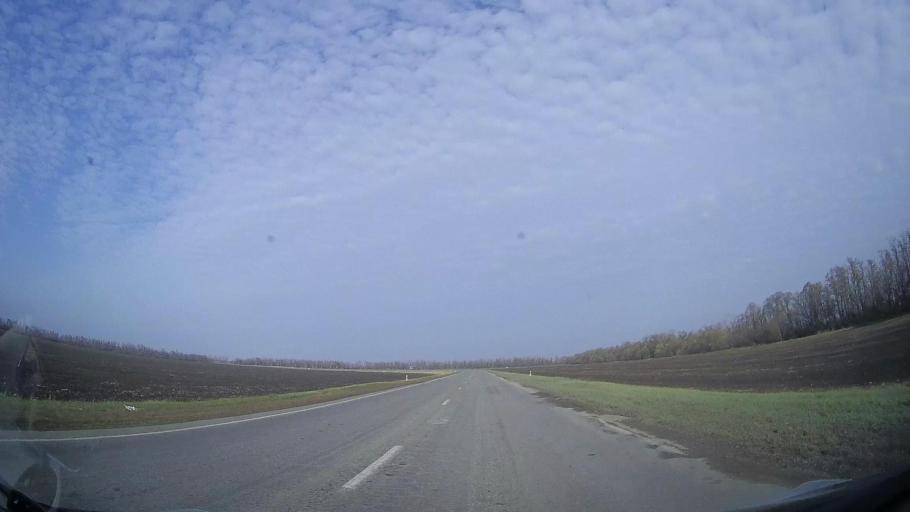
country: RU
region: Rostov
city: Tselina
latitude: 46.5245
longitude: 40.9915
